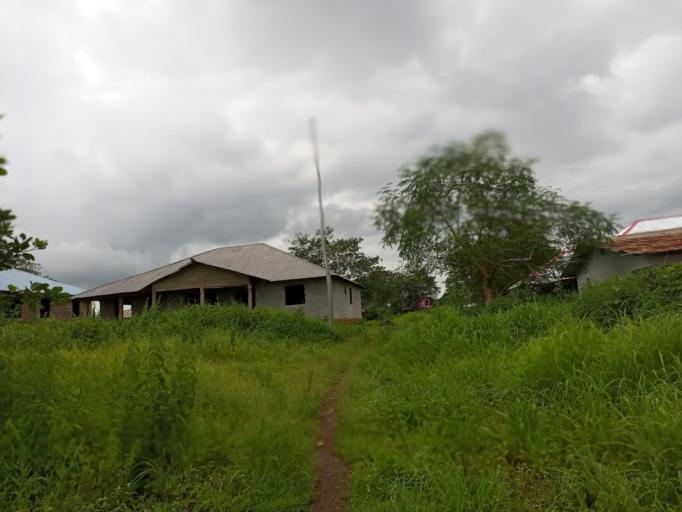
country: SL
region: Northern Province
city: Kamakwie
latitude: 9.5013
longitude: -12.2536
